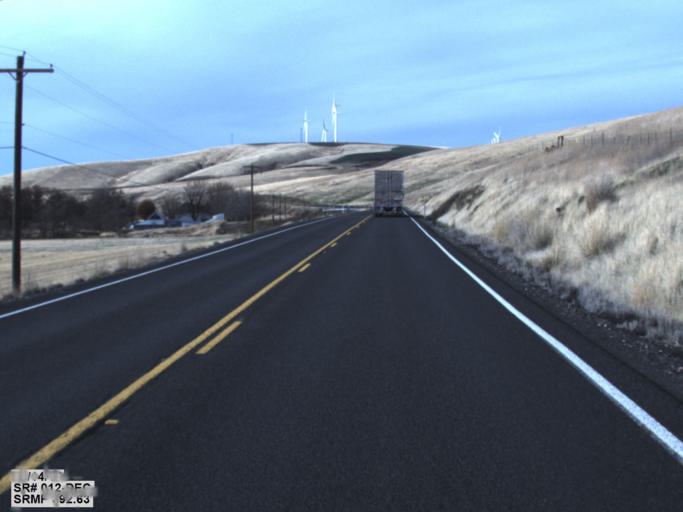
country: US
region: Washington
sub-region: Garfield County
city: Pomeroy
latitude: 46.5143
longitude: -117.7888
